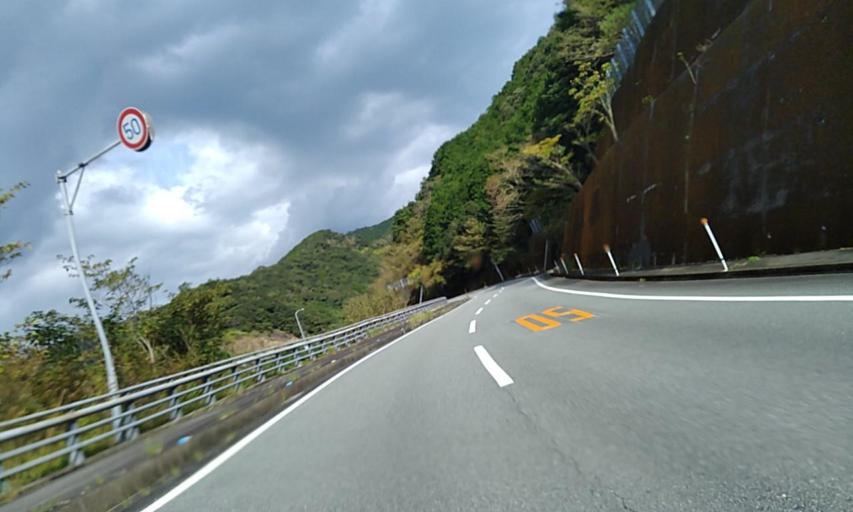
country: JP
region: Mie
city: Owase
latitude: 34.2441
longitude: 136.4005
